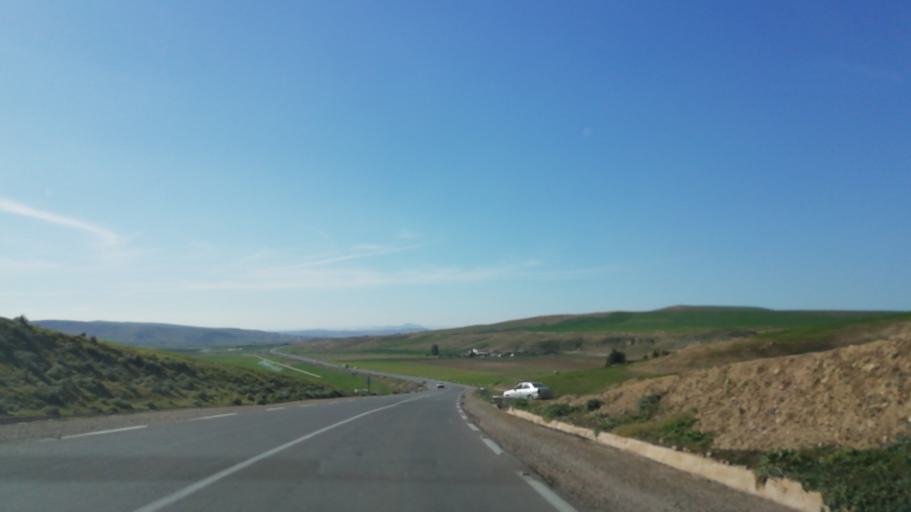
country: DZ
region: Mascara
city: Oued el Abtal
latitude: 35.4490
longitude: 0.8082
